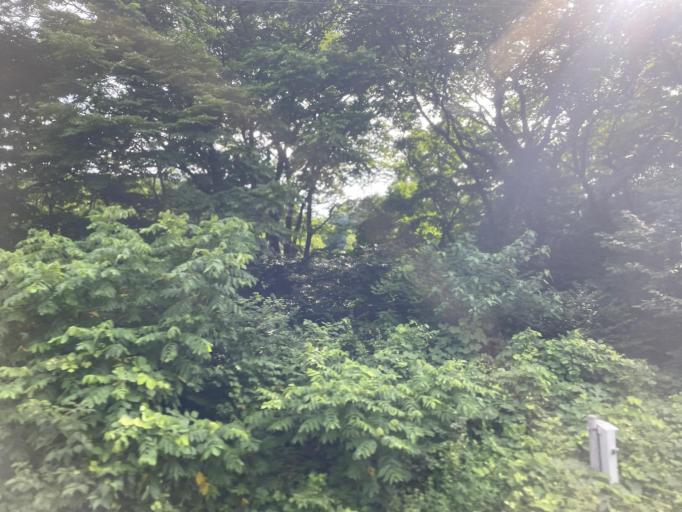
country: JP
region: Gunma
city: Numata
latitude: 36.7487
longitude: 138.9803
